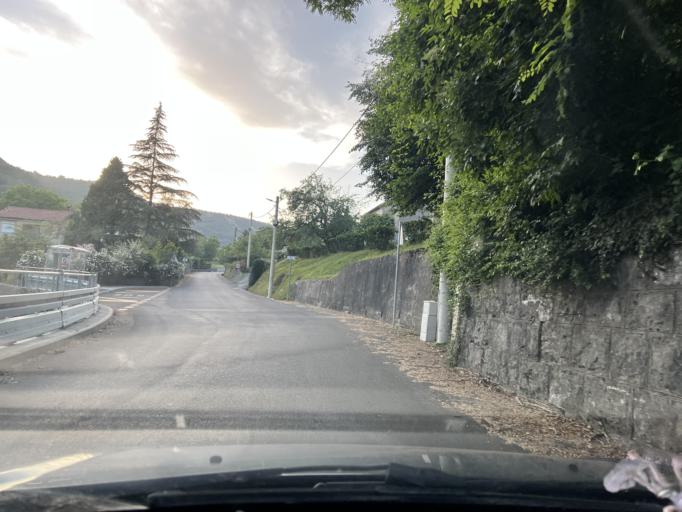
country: HR
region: Primorsko-Goranska
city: Marcelji
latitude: 45.3957
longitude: 14.4261
